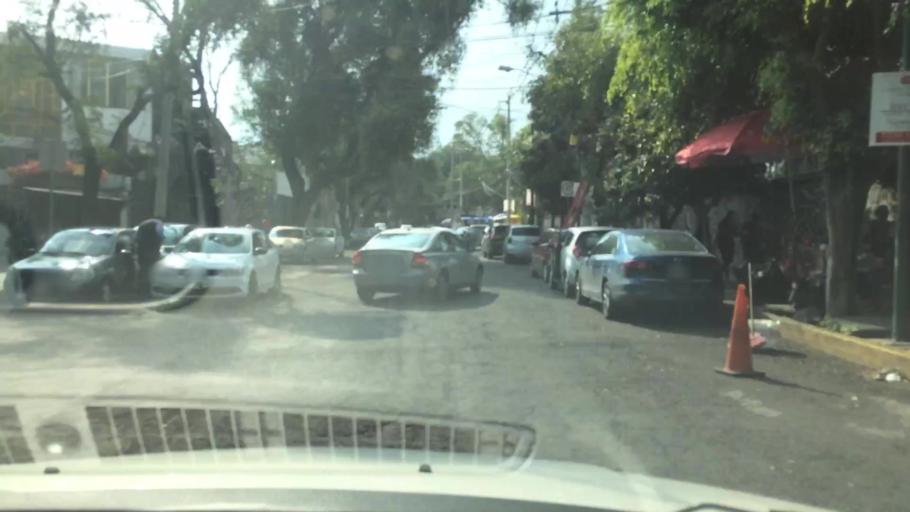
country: MX
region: Mexico City
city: Tlalpan
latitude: 19.2965
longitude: -99.1595
